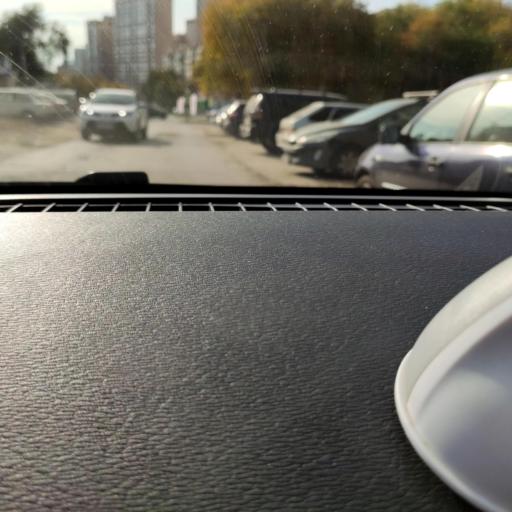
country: RU
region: Samara
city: Samara
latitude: 53.1938
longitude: 50.1403
